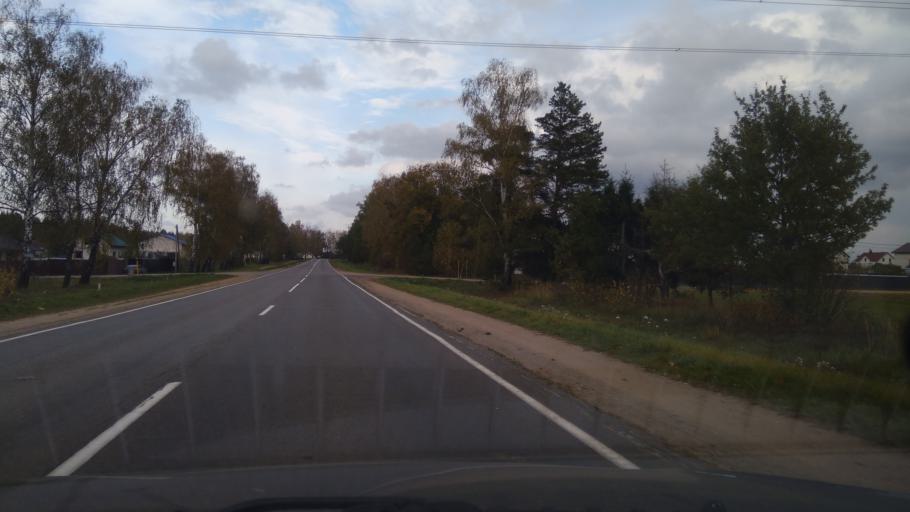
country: BY
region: Minsk
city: Svislach
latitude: 53.6508
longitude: 27.9286
